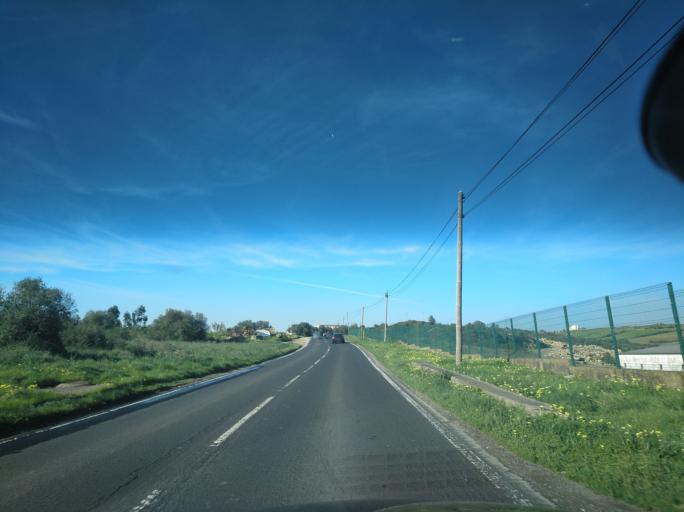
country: PT
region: Lisbon
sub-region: Mafra
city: Mafra
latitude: 38.9024
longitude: -9.3279
